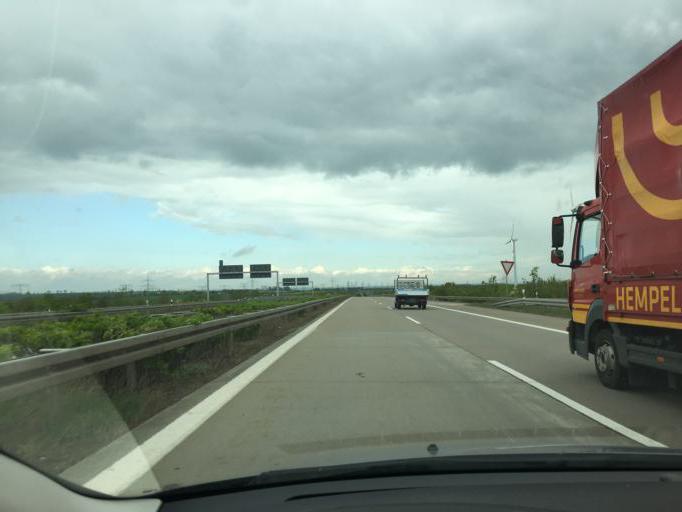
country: DE
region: Saxony-Anhalt
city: Dahlenwarsleben
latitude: 52.1708
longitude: 11.5458
